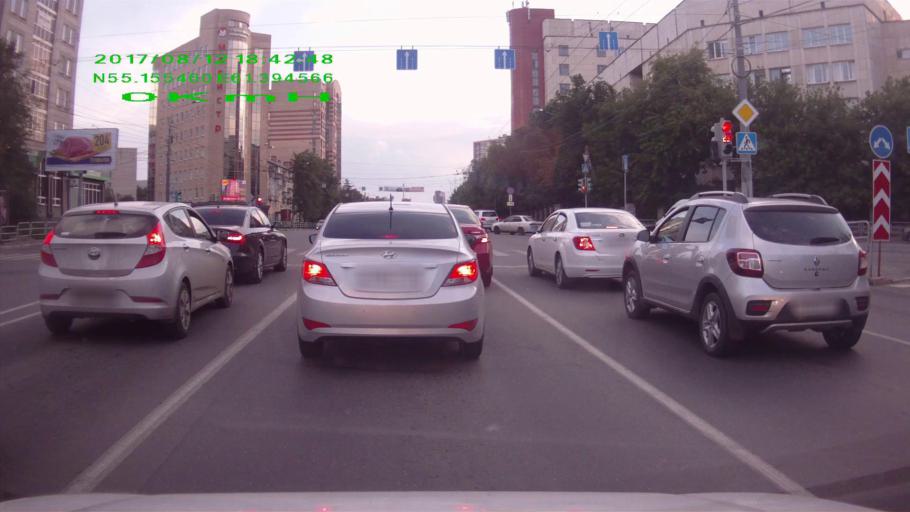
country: RU
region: Chelyabinsk
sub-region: Gorod Chelyabinsk
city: Chelyabinsk
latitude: 55.1547
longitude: 61.3935
